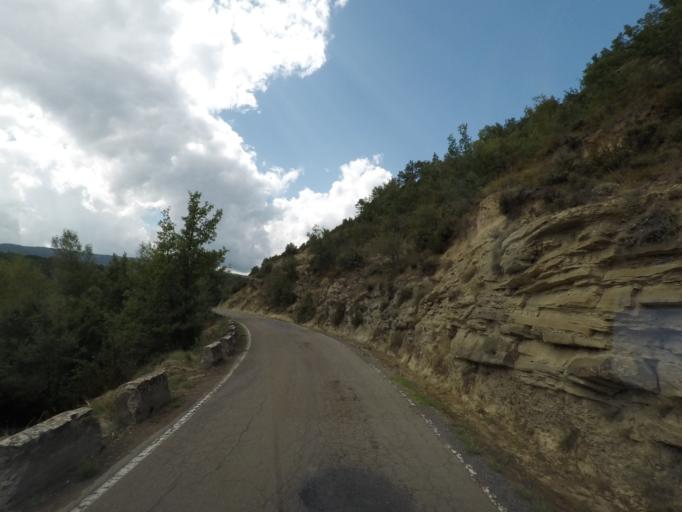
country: ES
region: Aragon
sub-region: Provincia de Huesca
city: Yebra de Basa
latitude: 42.3907
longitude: -0.2795
